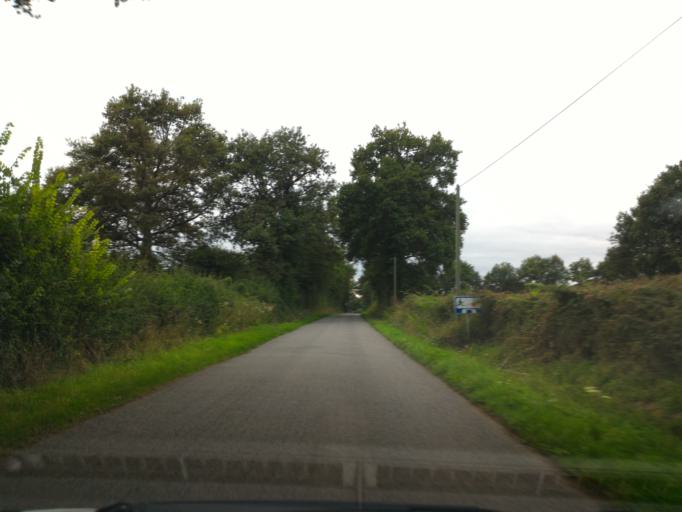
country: FR
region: Poitou-Charentes
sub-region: Departement de la Charente
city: Etagnac
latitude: 45.9474
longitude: 0.7899
